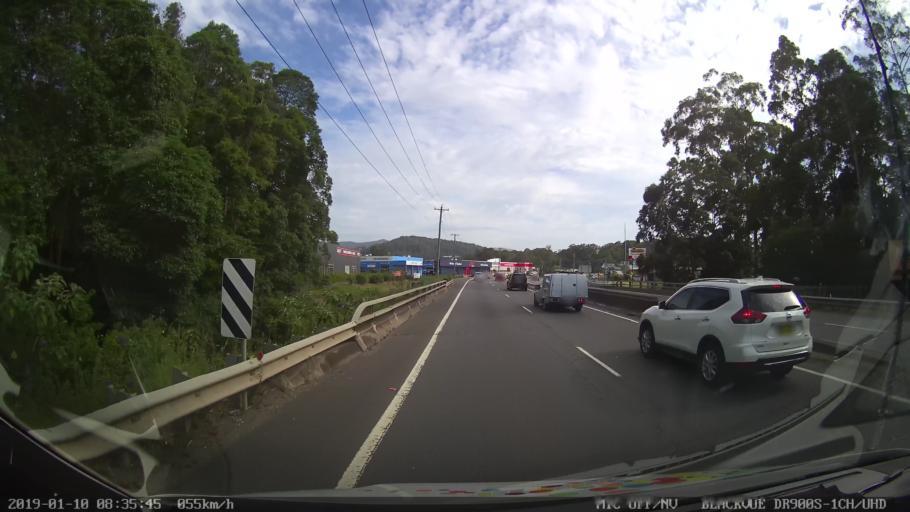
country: AU
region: New South Wales
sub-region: Coffs Harbour
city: Coffs Harbour
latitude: -30.3157
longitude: 153.0918
